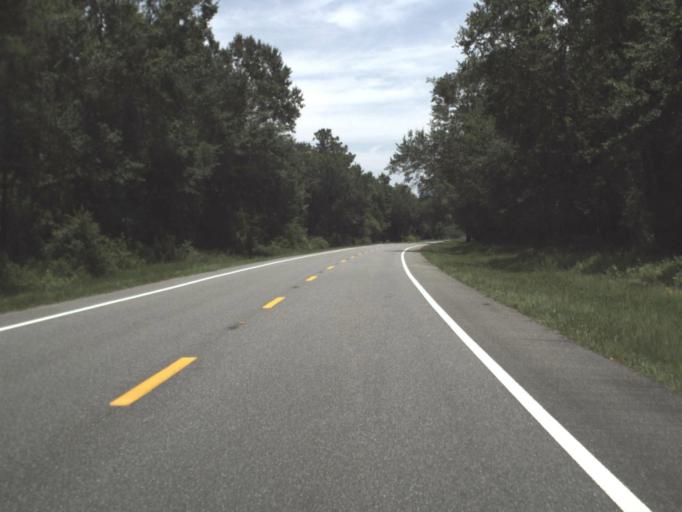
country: US
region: Florida
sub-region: Lafayette County
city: Mayo
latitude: 29.9165
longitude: -83.2880
